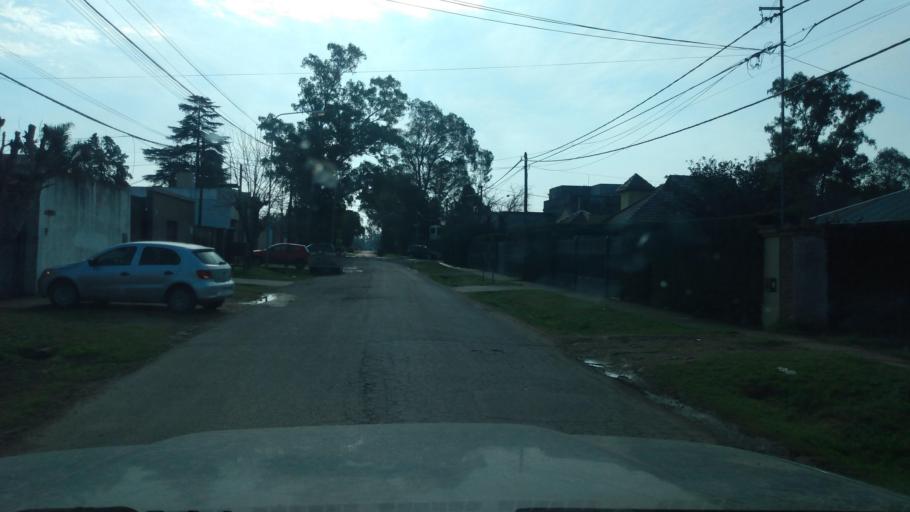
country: AR
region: Buenos Aires
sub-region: Partido de Lujan
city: Lujan
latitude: -34.5722
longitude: -59.0861
